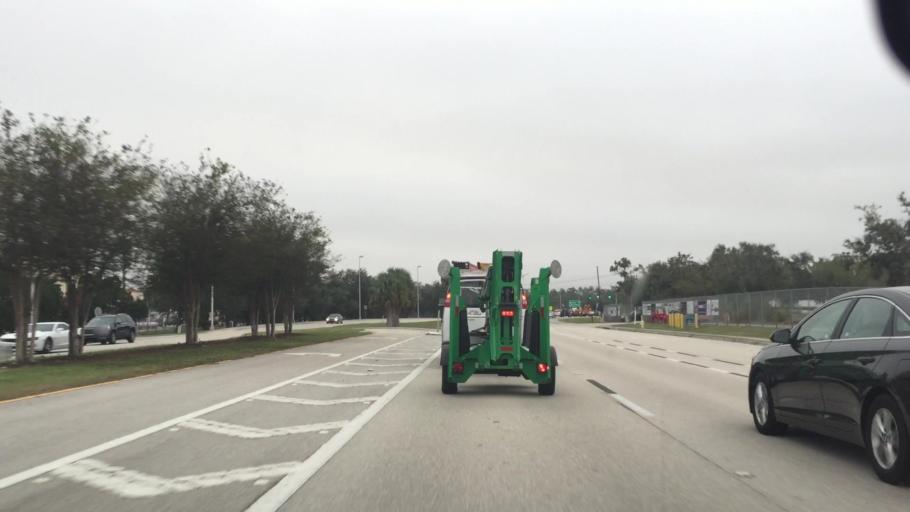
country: US
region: Florida
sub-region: Lee County
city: Three Oaks
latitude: 26.4726
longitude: -81.7947
